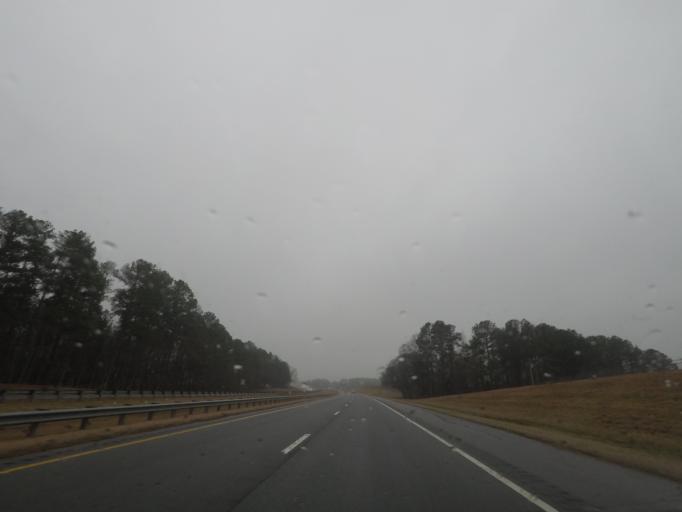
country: US
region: North Carolina
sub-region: Chatham County
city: Farmville
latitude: 35.5348
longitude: -79.1785
